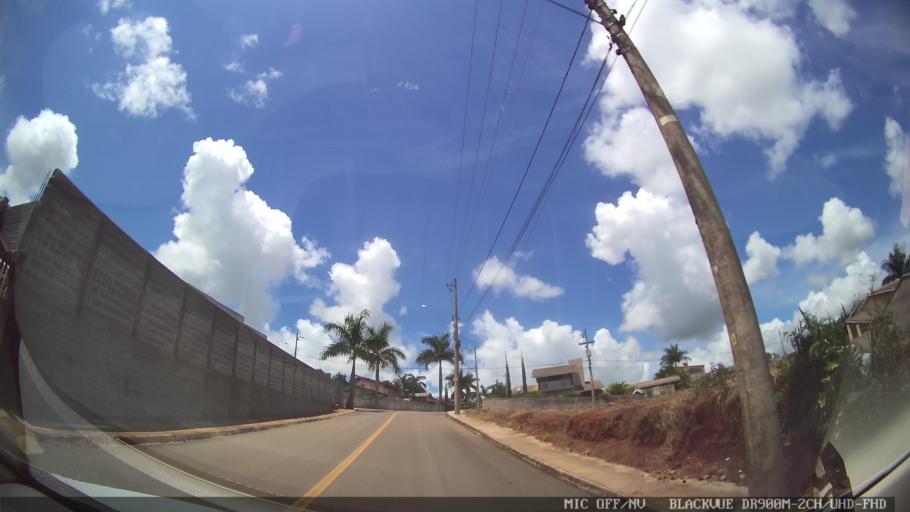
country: BR
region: Sao Paulo
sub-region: Amparo
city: Amparo
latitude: -22.8175
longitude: -46.6937
